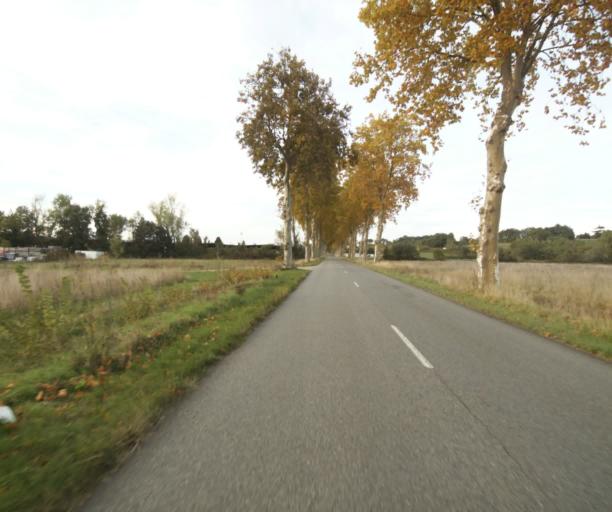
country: FR
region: Midi-Pyrenees
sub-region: Departement du Tarn-et-Garonne
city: Grisolles
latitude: 43.8431
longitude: 1.2942
